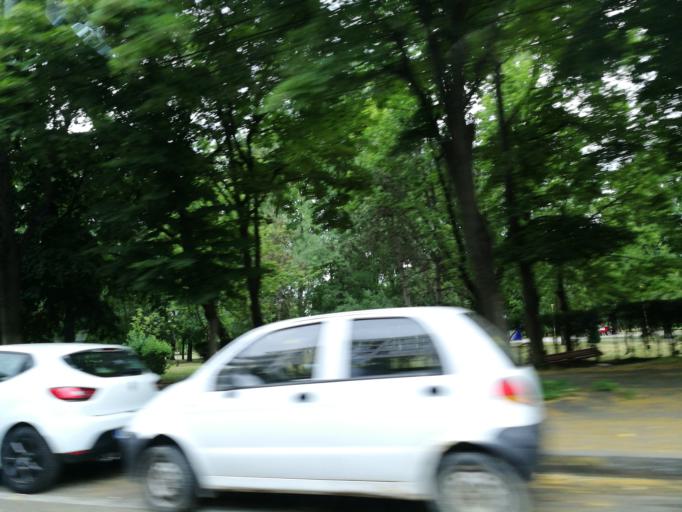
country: RO
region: Constanta
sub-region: Municipiul Constanta
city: Constanta
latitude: 44.2051
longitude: 28.6298
